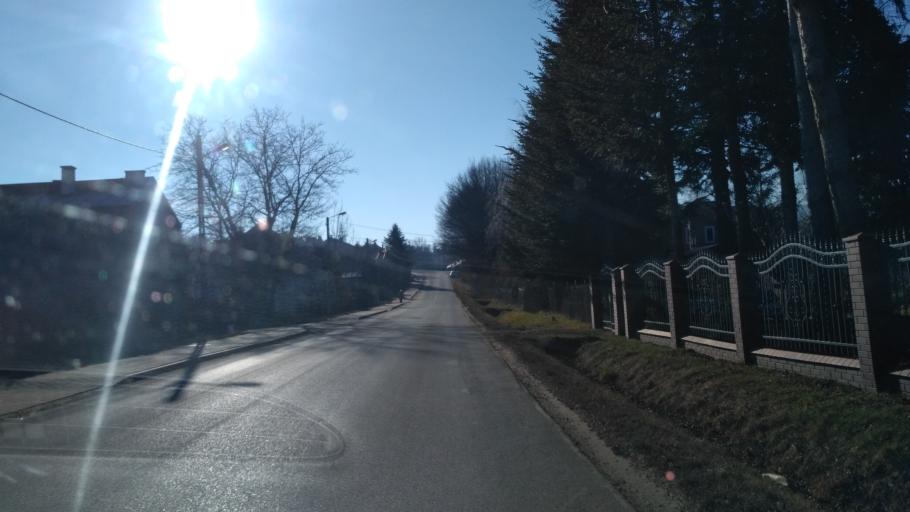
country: PL
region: Subcarpathian Voivodeship
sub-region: Powiat krosnienski
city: Rymanow
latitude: 49.5792
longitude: 21.8642
